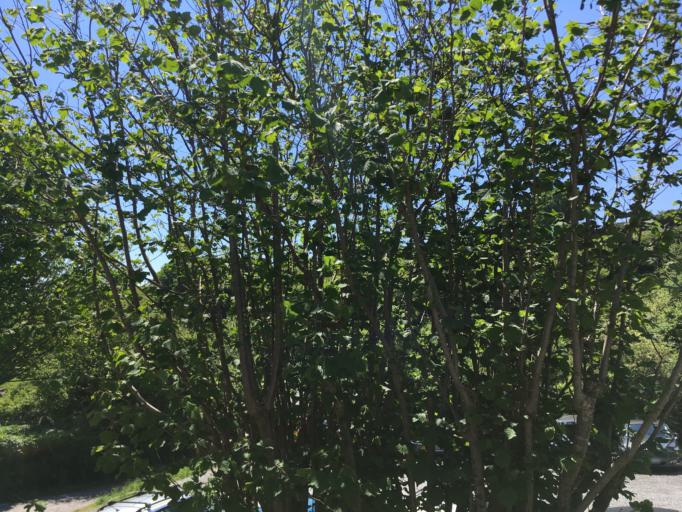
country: GB
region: England
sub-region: Devon
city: Dartmouth
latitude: 50.3477
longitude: -3.5366
